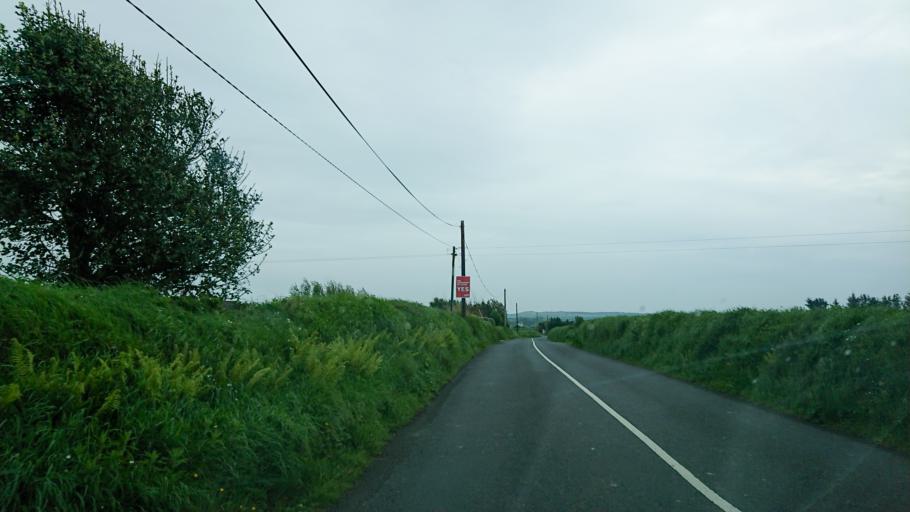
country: IE
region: Munster
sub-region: Waterford
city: Waterford
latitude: 52.2236
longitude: -7.0538
